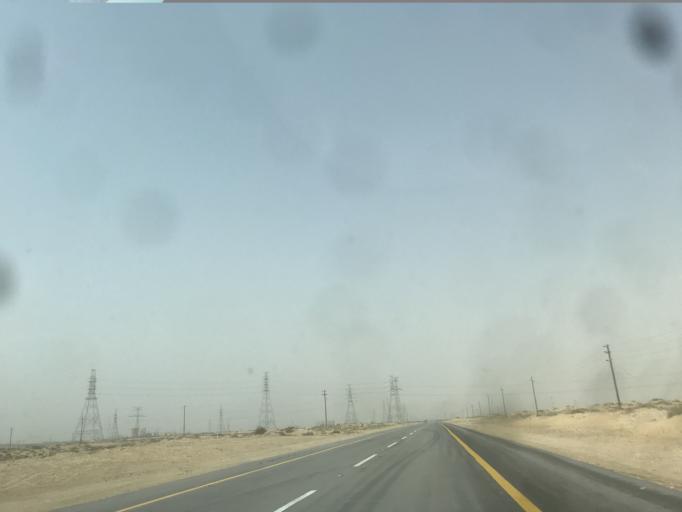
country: SA
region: Eastern Province
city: Abqaiq
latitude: 25.9369
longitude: 49.7242
